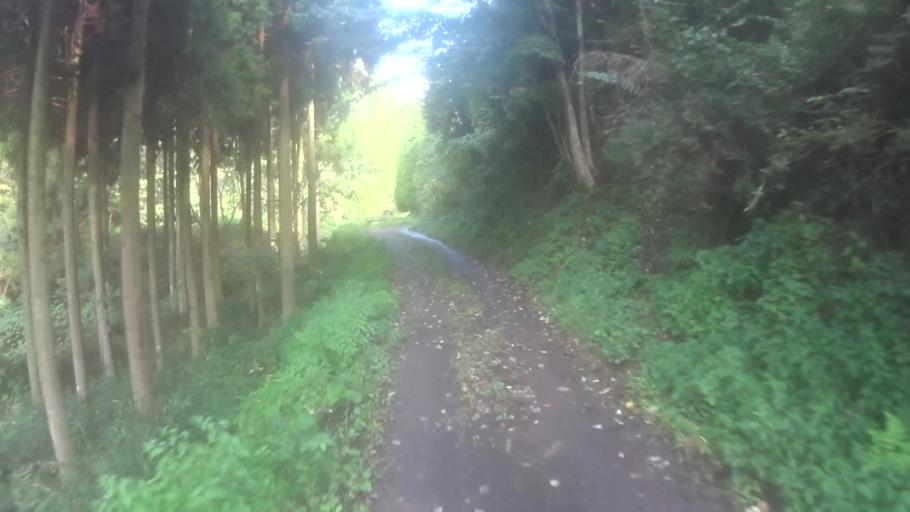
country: JP
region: Kyoto
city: Miyazu
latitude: 35.6195
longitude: 135.1551
